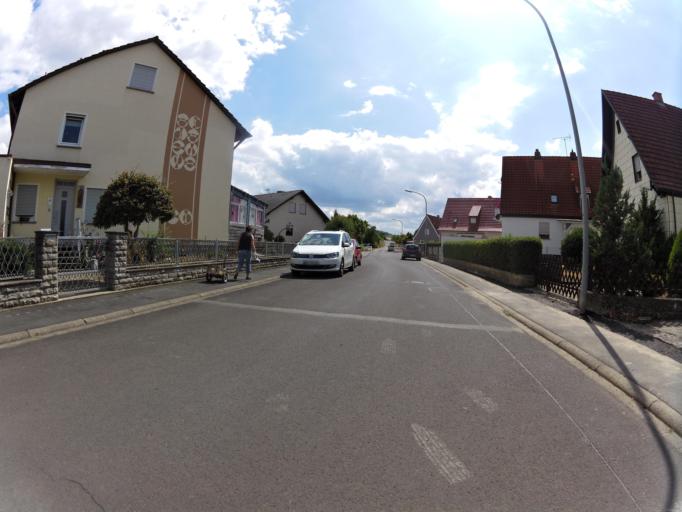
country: DE
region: Bavaria
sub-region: Regierungsbezirk Unterfranken
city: Zellingen
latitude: 49.8935
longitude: 9.8169
